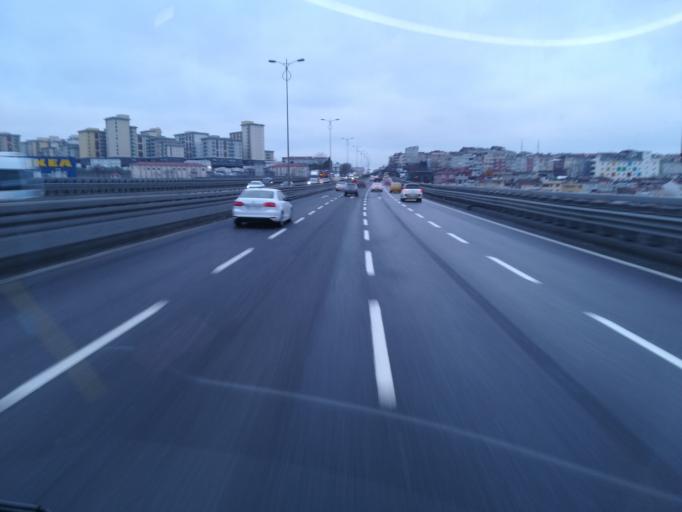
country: TR
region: Istanbul
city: Esenler
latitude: 41.0436
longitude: 28.8951
